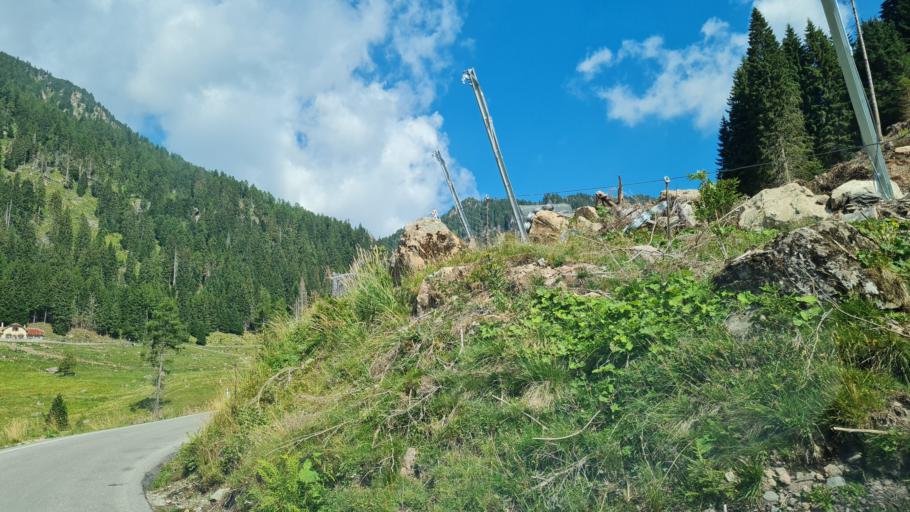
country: IT
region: Trentino-Alto Adige
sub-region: Provincia di Trento
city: Torcegno
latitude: 46.1566
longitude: 11.4372
